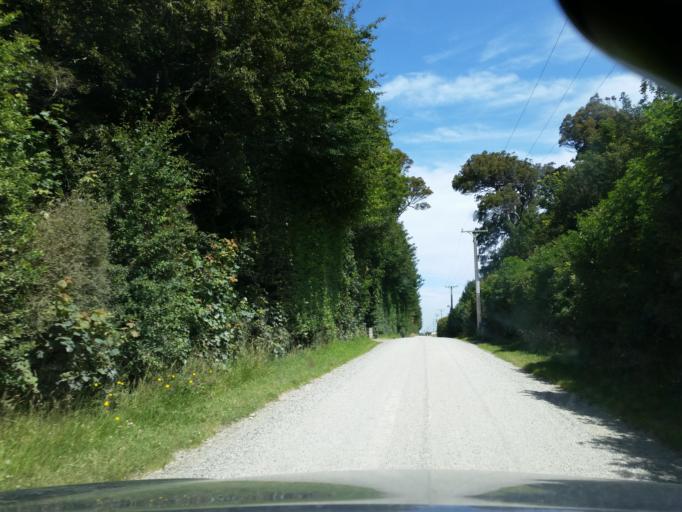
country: NZ
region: Southland
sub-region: Invercargill City
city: Invercargill
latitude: -46.3217
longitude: 168.4789
